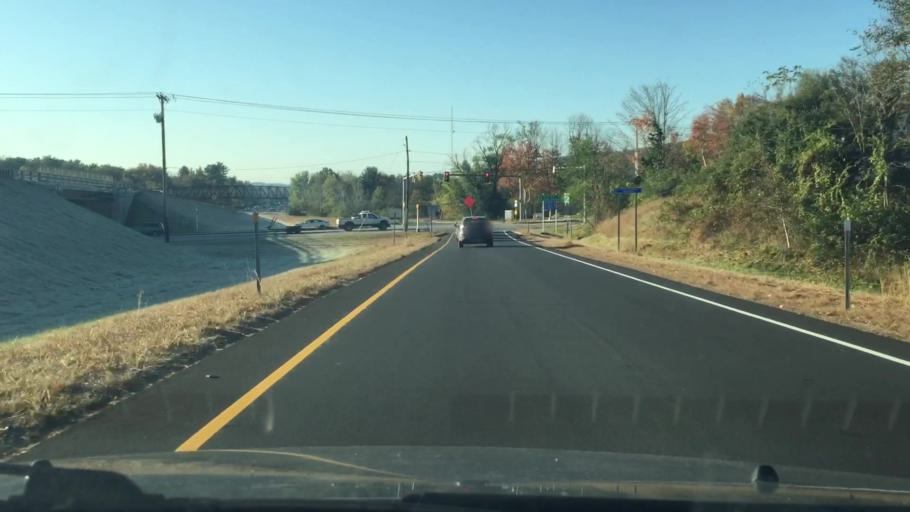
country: US
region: New Hampshire
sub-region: Cheshire County
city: Keene
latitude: 42.9347
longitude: -72.2978
